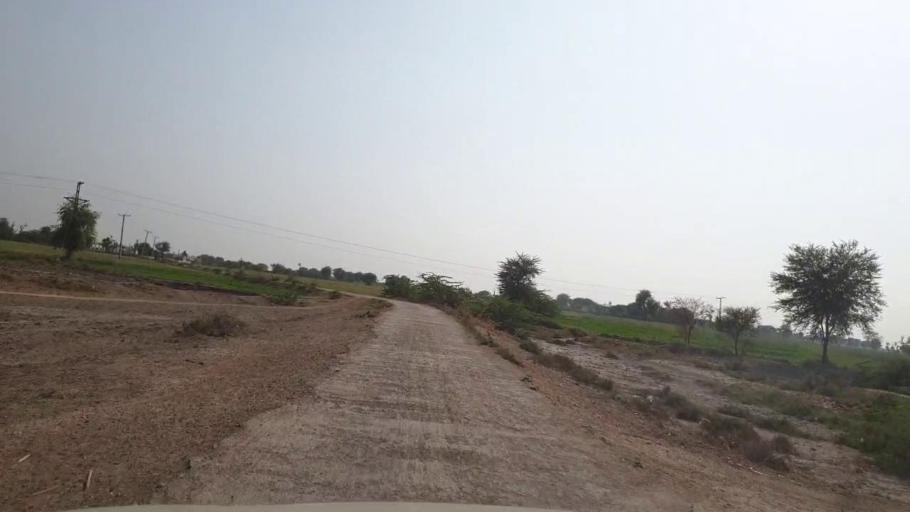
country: PK
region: Sindh
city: Dhoro Naro
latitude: 25.4757
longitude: 69.6464
